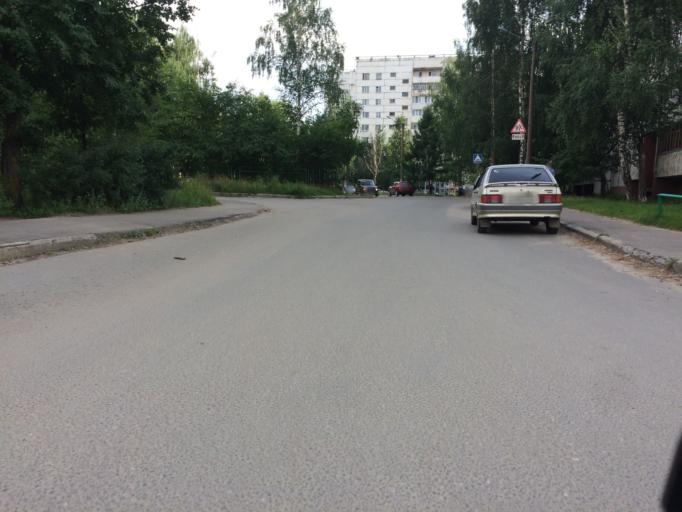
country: RU
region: Mariy-El
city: Yoshkar-Ola
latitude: 56.6303
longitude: 47.9107
